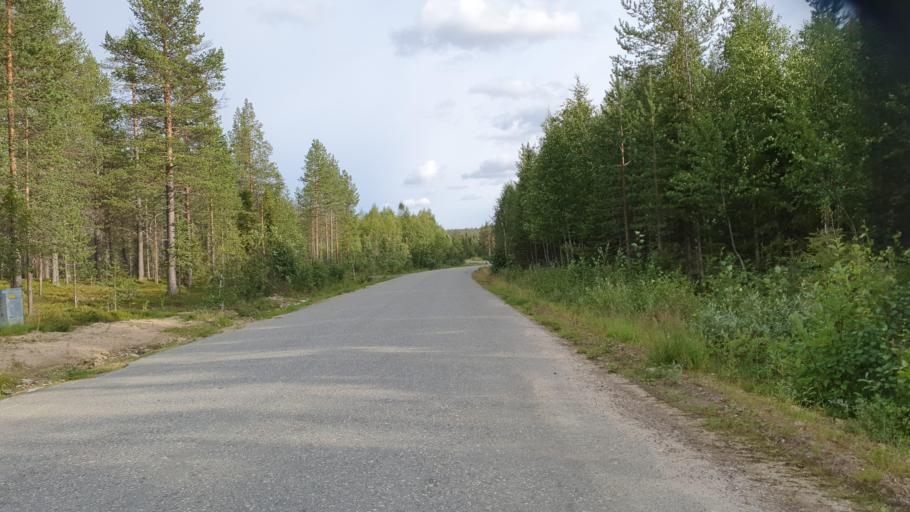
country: FI
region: Lapland
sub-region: Tunturi-Lappi
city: Kolari
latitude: 67.6001
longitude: 24.1638
